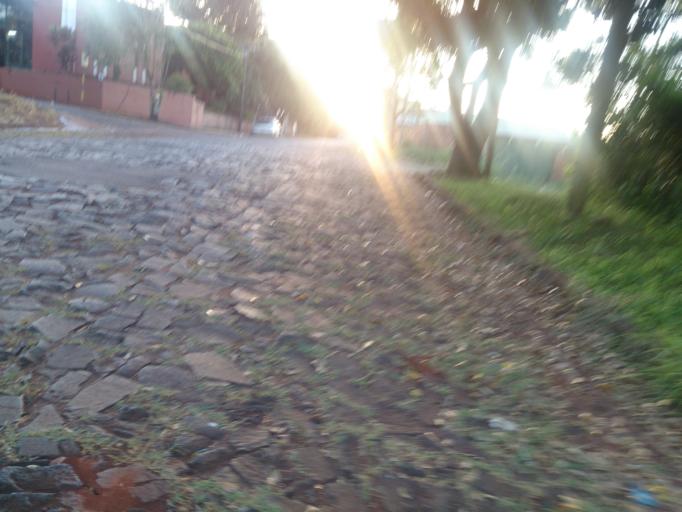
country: AR
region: Misiones
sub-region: Departamento de Obera
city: Obera
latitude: -27.4947
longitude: -55.1191
